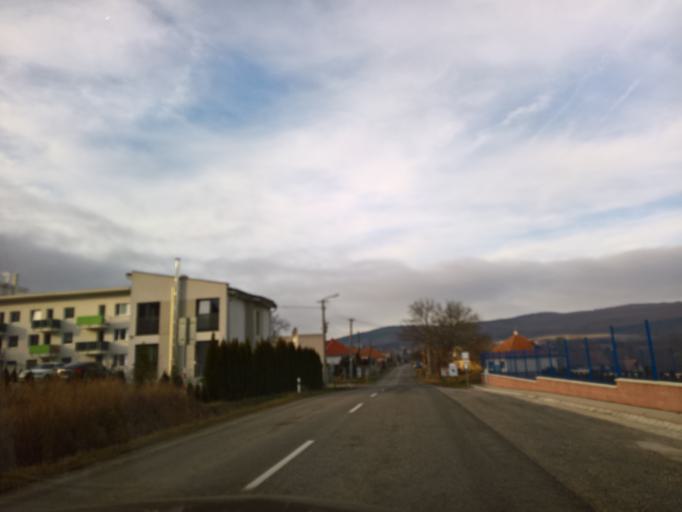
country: SK
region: Nitriansky
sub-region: Okres Nitra
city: Nitra
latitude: 48.3717
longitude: 18.1812
